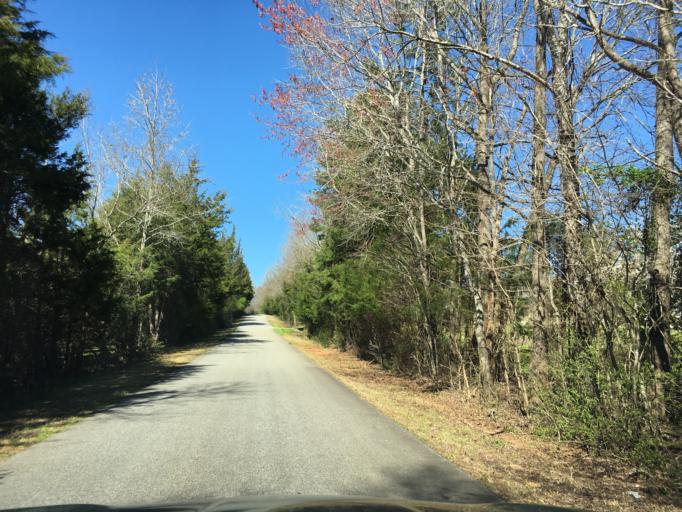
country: US
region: South Carolina
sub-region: Spartanburg County
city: Woodruff
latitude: 34.7967
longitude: -82.0863
